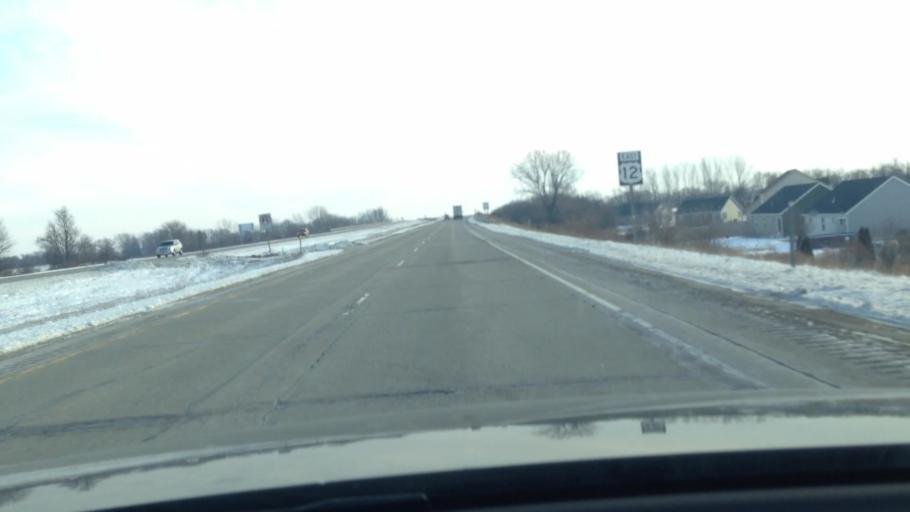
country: US
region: Wisconsin
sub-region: Walworth County
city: Elkhorn
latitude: 42.6603
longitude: -88.5121
